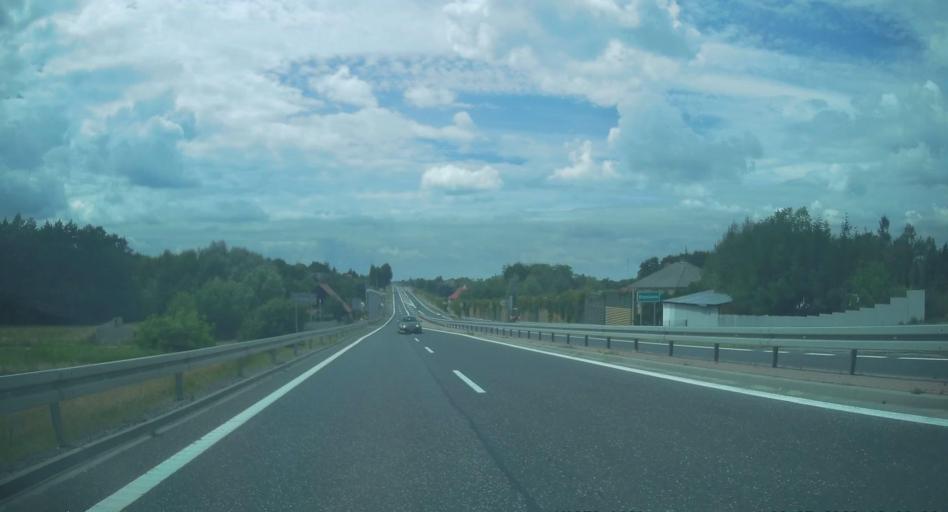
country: PL
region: Subcarpathian Voivodeship
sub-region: Powiat ropczycko-sedziszowski
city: Ostrow
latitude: 50.0619
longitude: 21.5523
